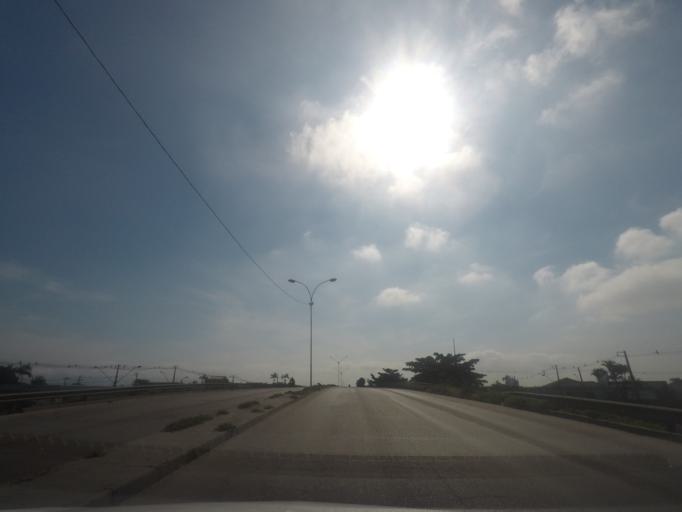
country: BR
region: Parana
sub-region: Paranagua
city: Paranagua
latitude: -25.5262
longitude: -48.5272
